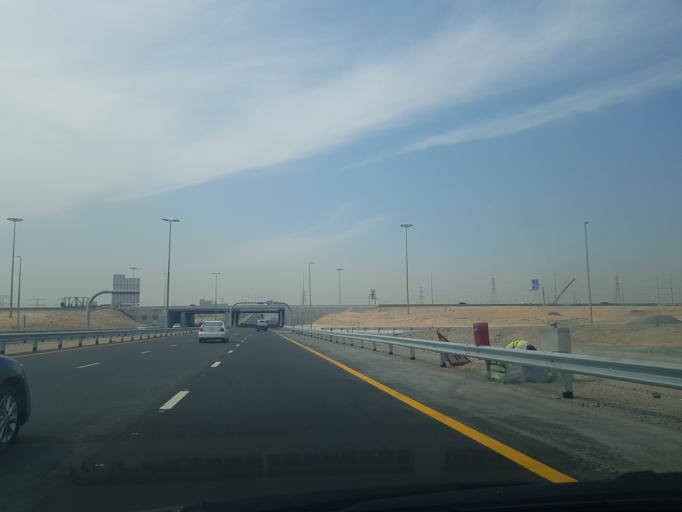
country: AE
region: Ash Shariqah
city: Sharjah
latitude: 25.2376
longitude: 55.5687
